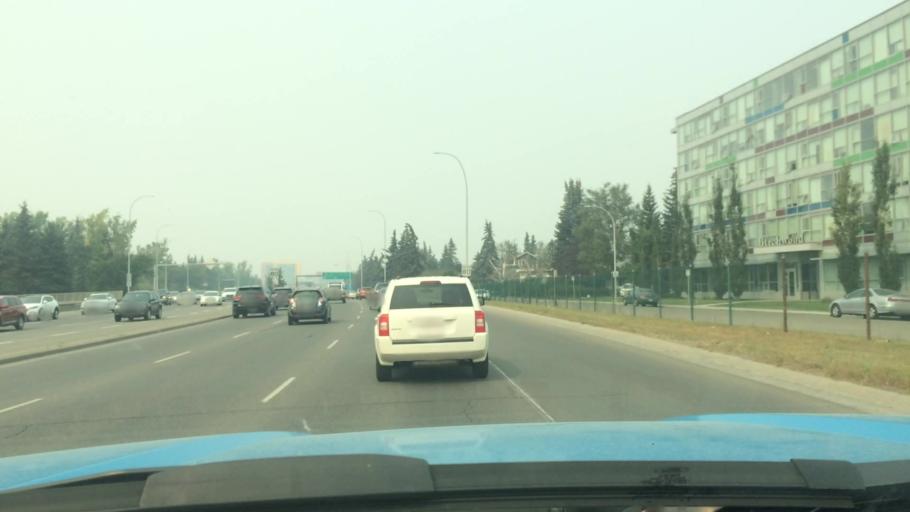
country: CA
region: Alberta
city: Calgary
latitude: 51.0749
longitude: -114.1185
